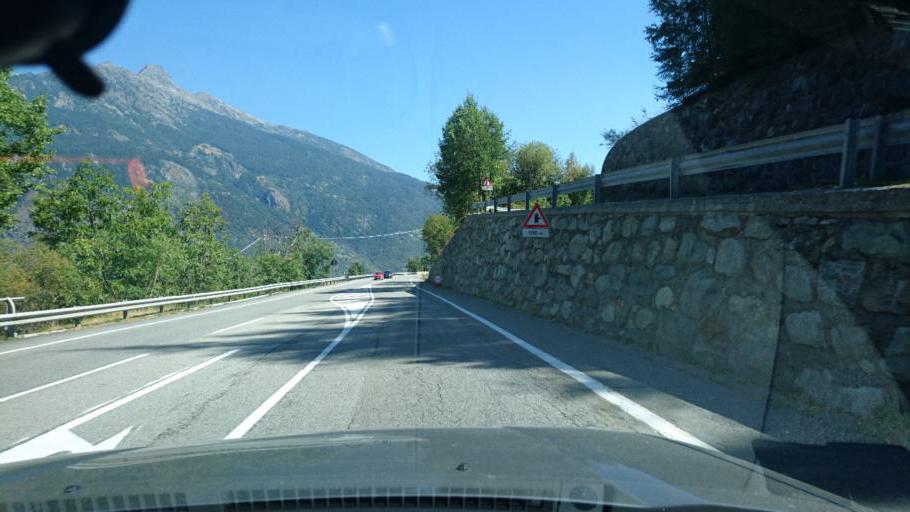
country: IT
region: Aosta Valley
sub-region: Valle d'Aosta
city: Allein
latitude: 45.7966
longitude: 7.2810
